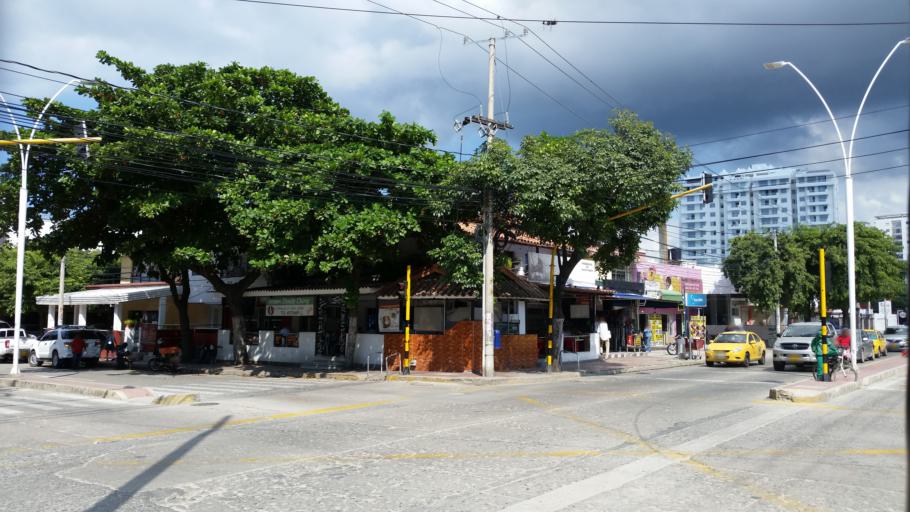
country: CO
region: Magdalena
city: Santa Marta
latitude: 11.2413
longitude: -74.1942
